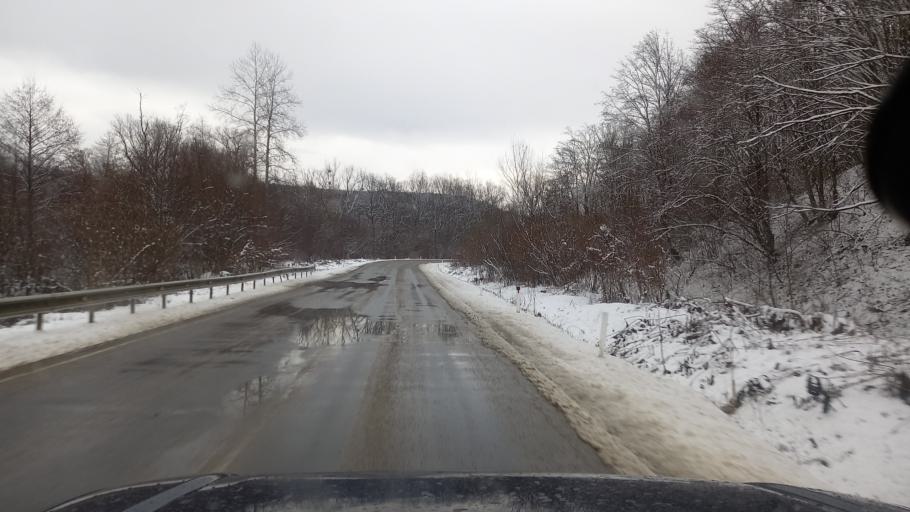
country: RU
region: Adygeya
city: Abadzekhskaya
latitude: 44.3660
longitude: 40.2714
